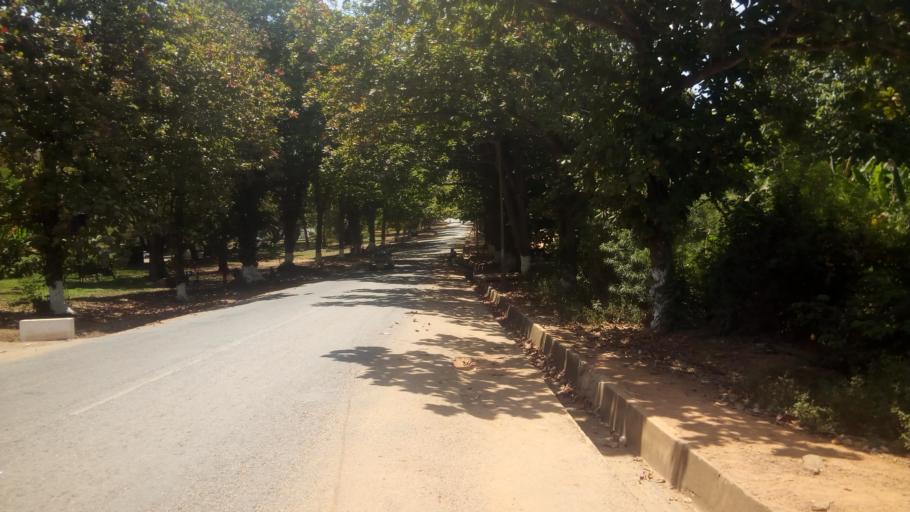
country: GH
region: Central
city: Cape Coast
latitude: 5.1091
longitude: -1.2864
